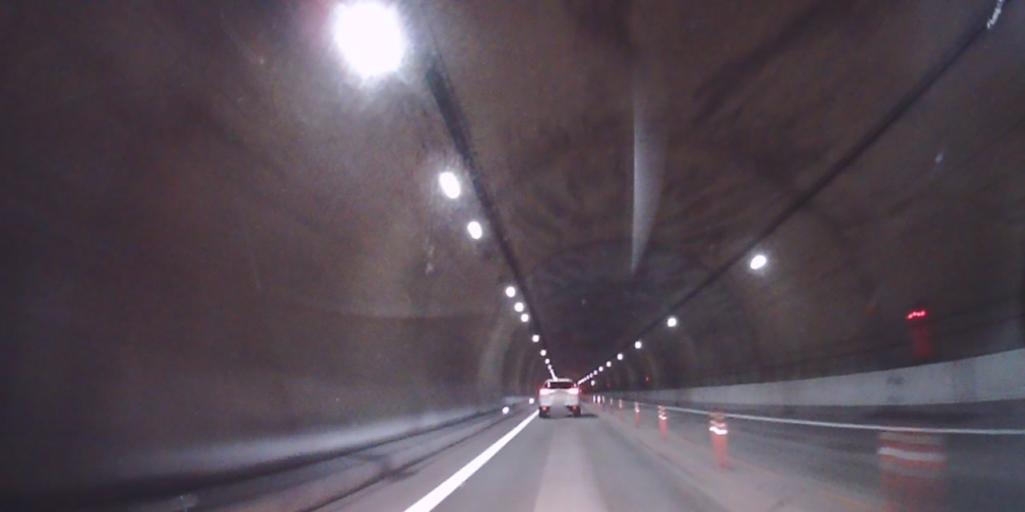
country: JP
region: Hokkaido
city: Date
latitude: 42.5738
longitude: 140.7430
